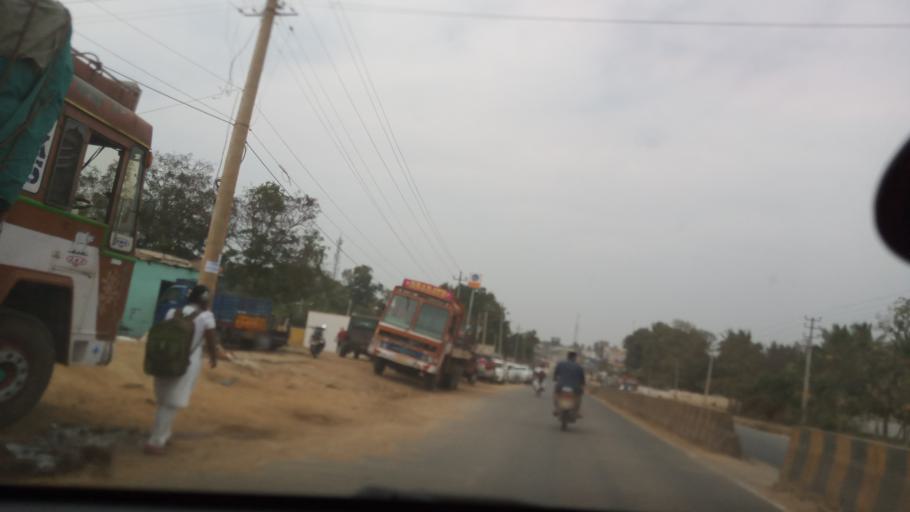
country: IN
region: Karnataka
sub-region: Chamrajnagar
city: Chamrajnagar
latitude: 11.9114
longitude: 76.9442
